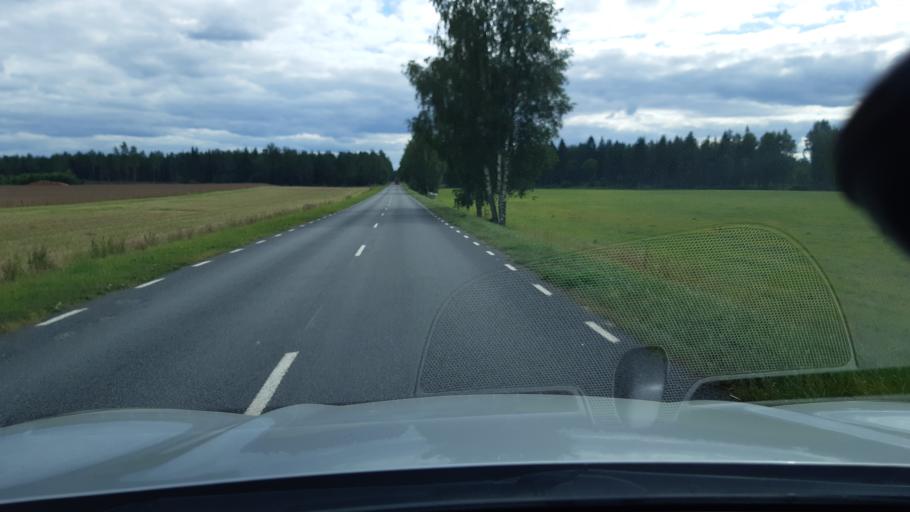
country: EE
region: Raplamaa
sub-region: Maerjamaa vald
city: Marjamaa
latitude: 59.0370
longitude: 24.5511
